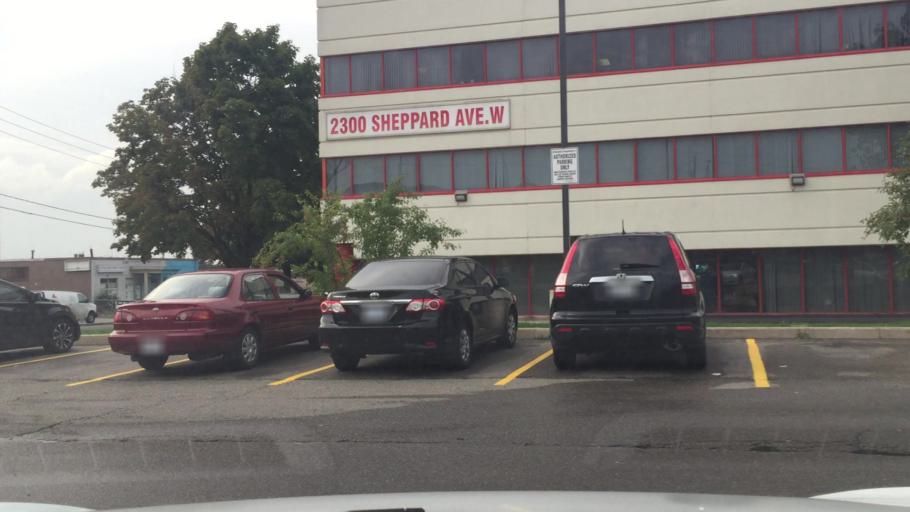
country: CA
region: Ontario
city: Concord
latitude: 43.7352
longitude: -79.5338
